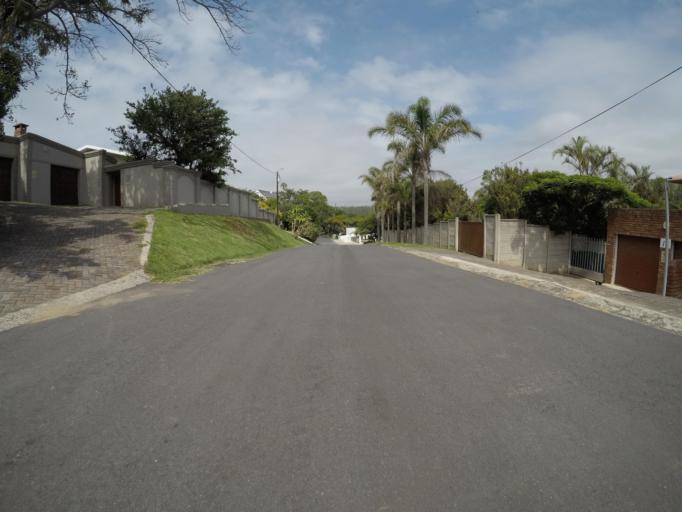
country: ZA
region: Eastern Cape
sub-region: Buffalo City Metropolitan Municipality
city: East London
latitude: -32.9339
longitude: 28.0270
